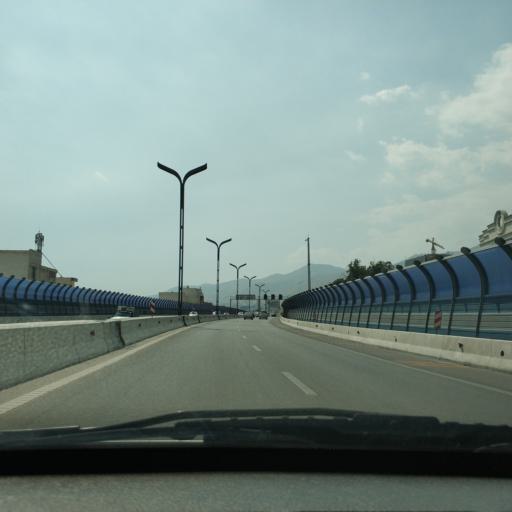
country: IR
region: Tehran
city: Tajrish
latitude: 35.7920
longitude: 51.4667
